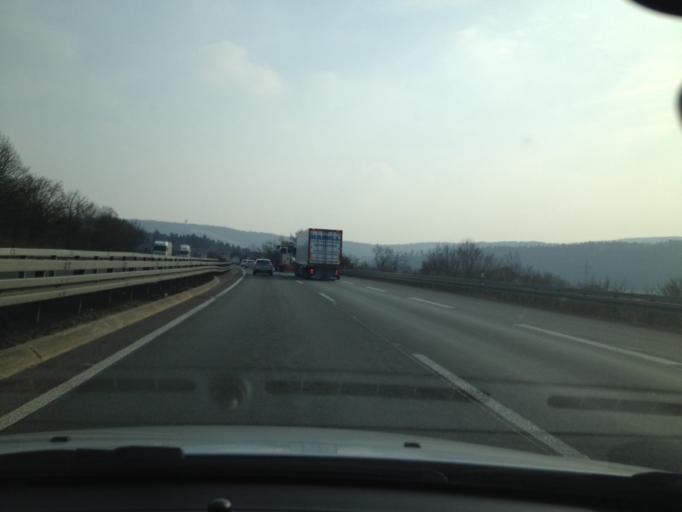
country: DE
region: Hesse
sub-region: Regierungsbezirk Giessen
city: Merkenbach
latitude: 50.6725
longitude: 8.2845
